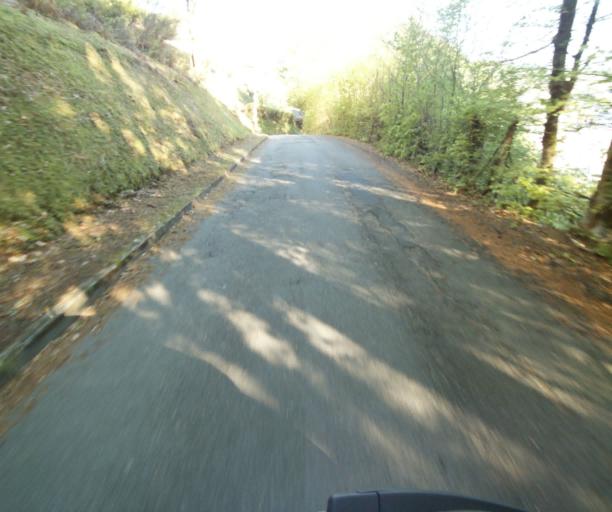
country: FR
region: Limousin
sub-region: Departement de la Correze
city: Tulle
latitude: 45.2604
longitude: 1.7686
